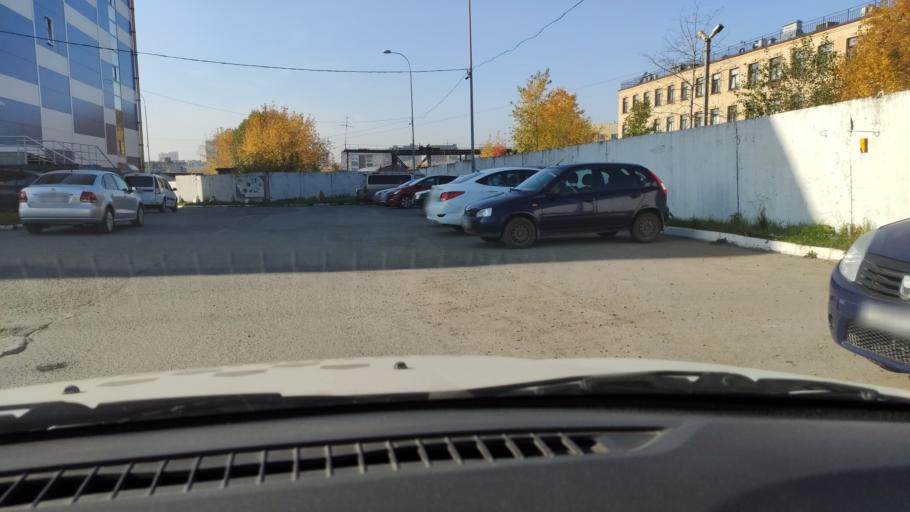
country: RU
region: Perm
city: Perm
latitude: 57.9805
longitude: 56.2409
